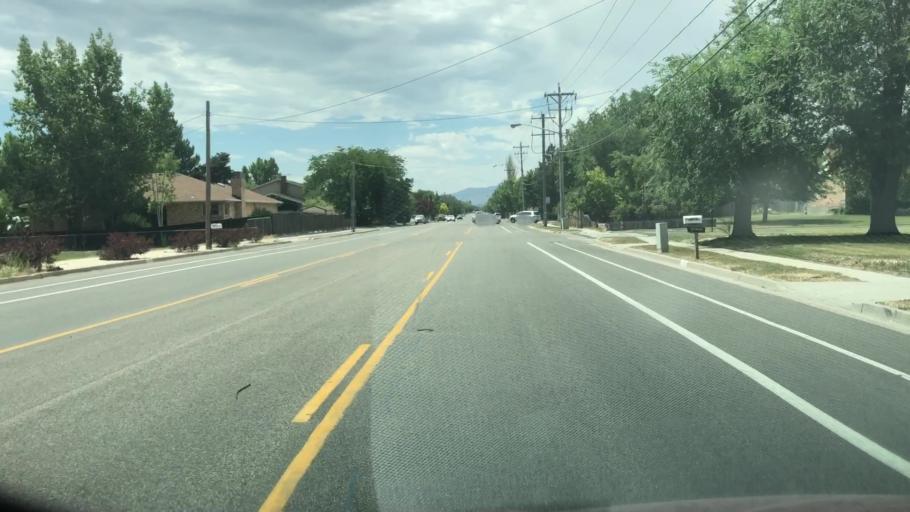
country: US
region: Utah
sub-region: Salt Lake County
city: South Jordan
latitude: 40.5565
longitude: -111.9292
